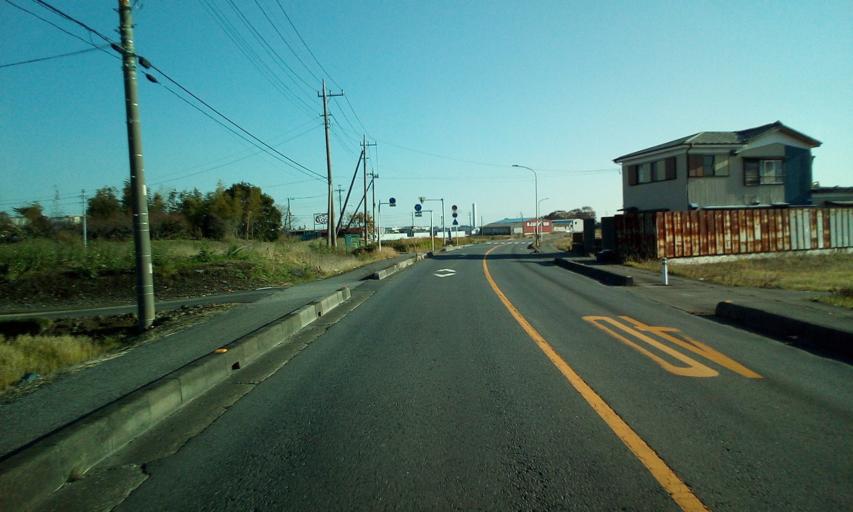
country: JP
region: Saitama
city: Yoshikawa
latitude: 35.8946
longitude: 139.8779
